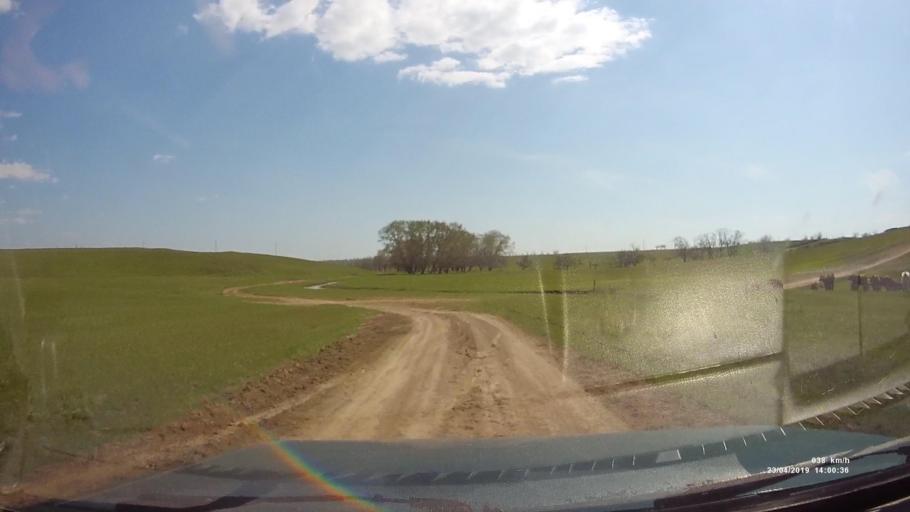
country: RU
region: Rostov
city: Remontnoye
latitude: 46.5586
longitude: 42.9469
